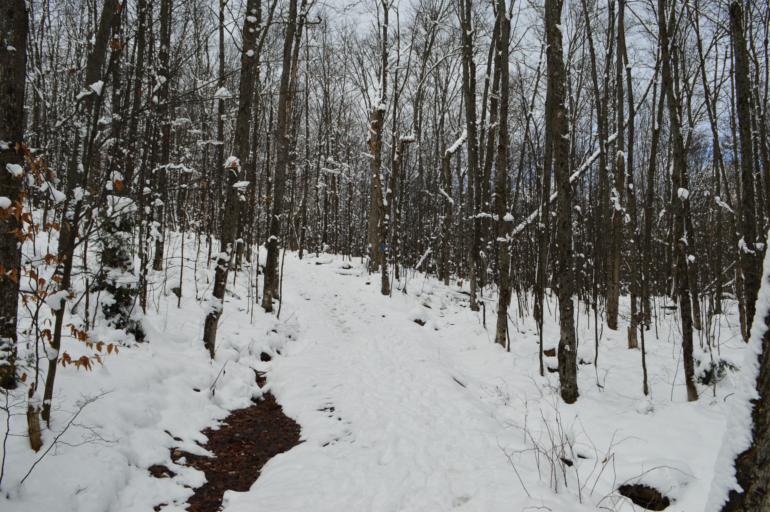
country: CA
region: Ontario
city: Bancroft
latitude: 45.5827
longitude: -78.4091
